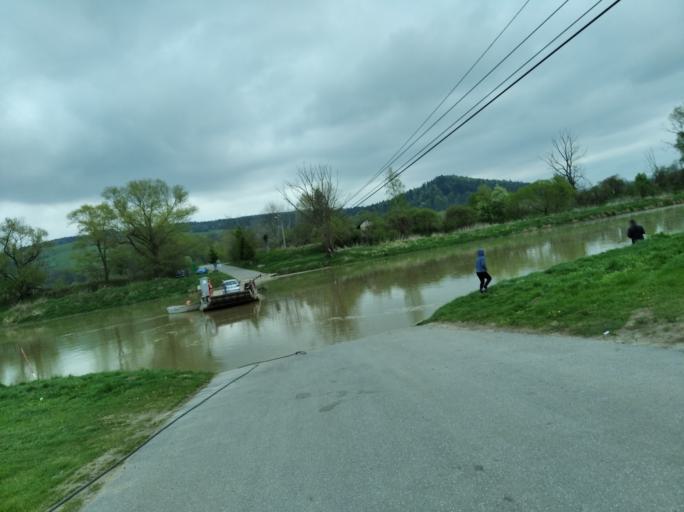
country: PL
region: Subcarpathian Voivodeship
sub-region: Powiat brzozowski
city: Dydnia
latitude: 49.7031
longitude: 22.2022
